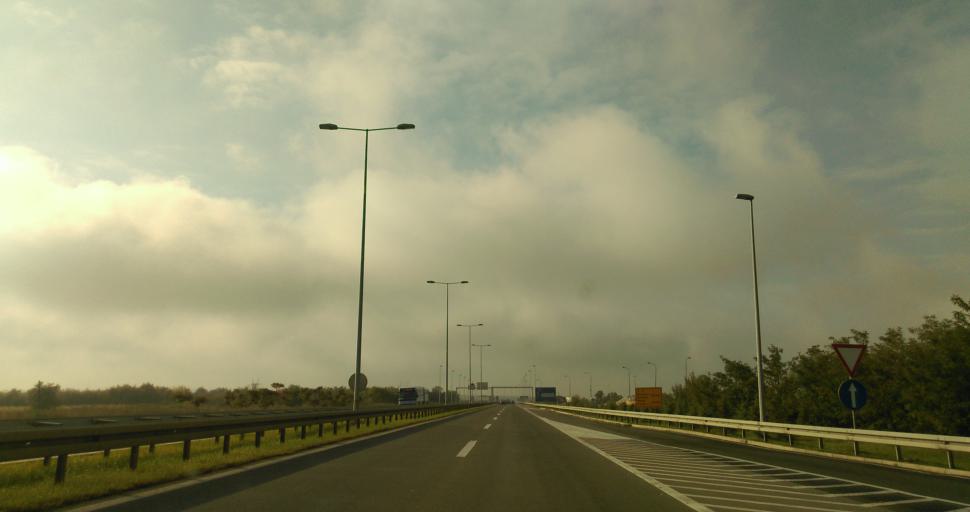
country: RS
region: Central Serbia
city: Sremcica
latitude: 44.7096
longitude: 20.4144
